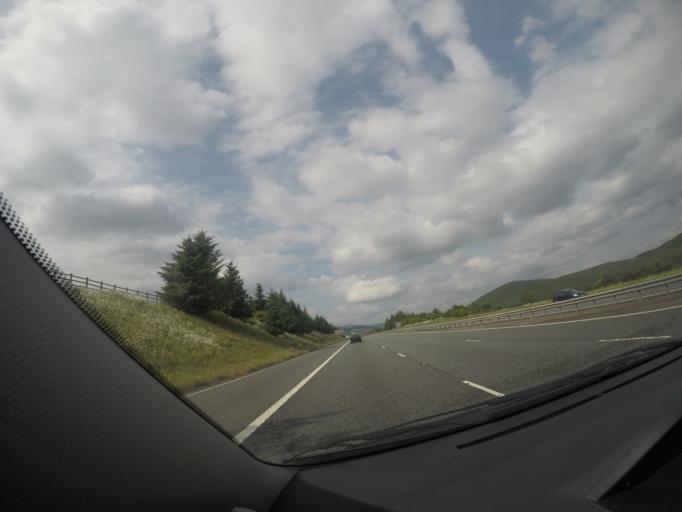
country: GB
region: Scotland
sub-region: South Lanarkshire
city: Douglas
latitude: 55.4954
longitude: -3.6954
